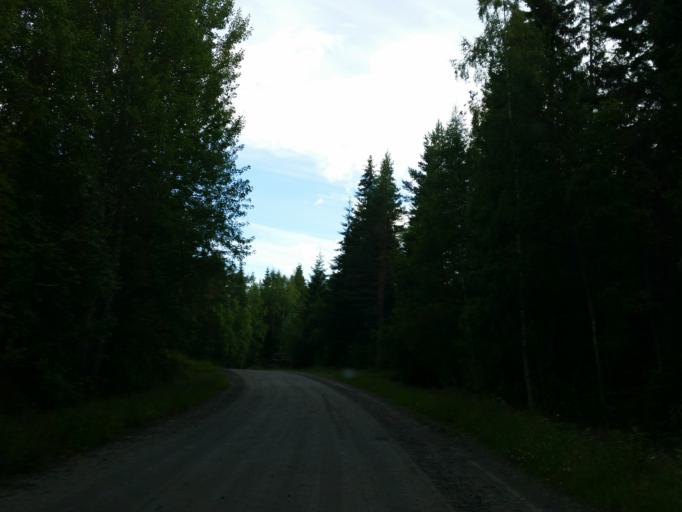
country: SE
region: Vaesterbotten
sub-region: Robertsfors Kommun
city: Robertsfors
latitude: 64.0457
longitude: 20.8507
